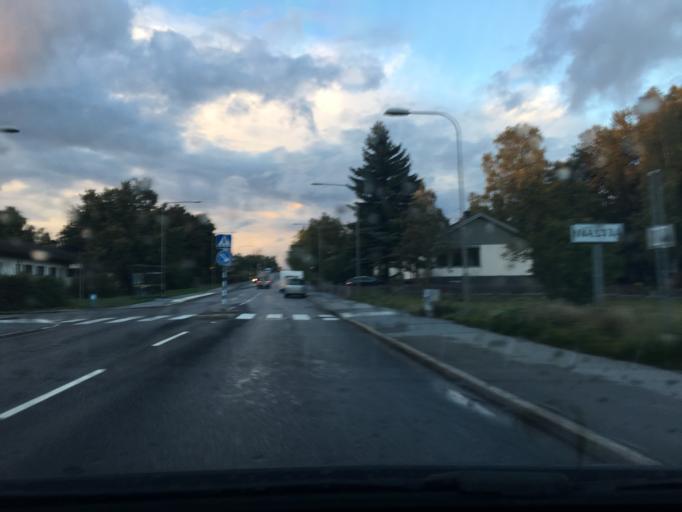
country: SE
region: Stockholm
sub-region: Jarfalla Kommun
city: Jakobsberg
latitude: 59.3739
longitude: 17.8692
